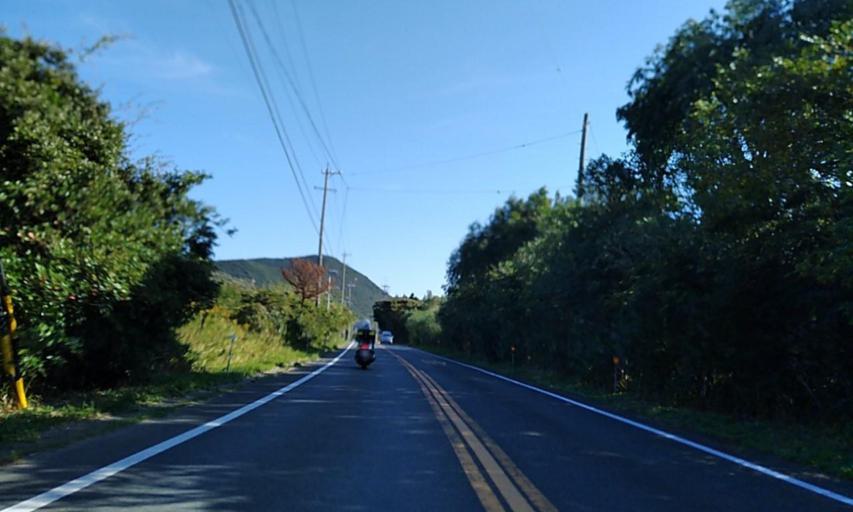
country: JP
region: Aichi
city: Toyohama
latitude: 34.5838
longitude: 137.0510
